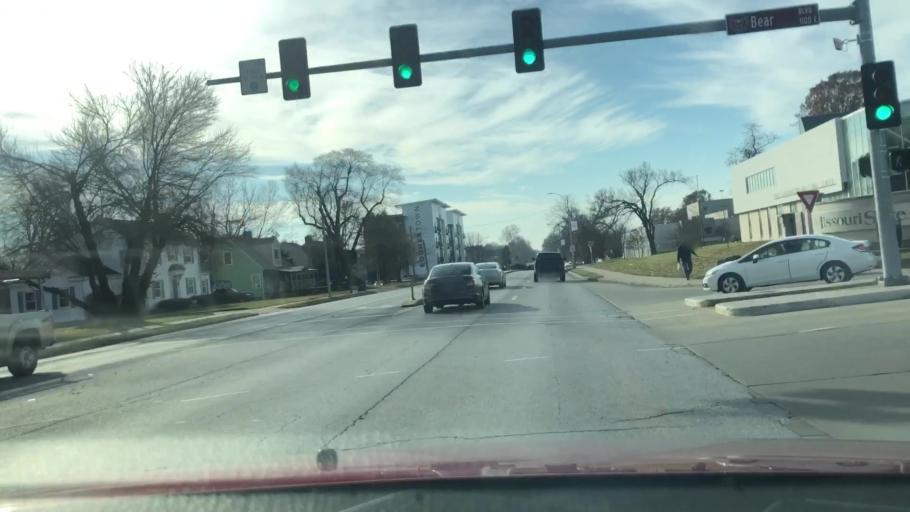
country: US
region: Missouri
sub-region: Greene County
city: Springfield
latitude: 37.2014
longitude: -93.2762
